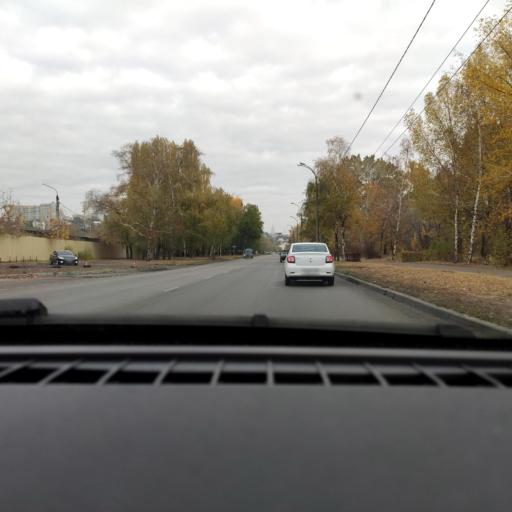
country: RU
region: Voronezj
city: Voronezh
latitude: 51.6474
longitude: 39.2113
